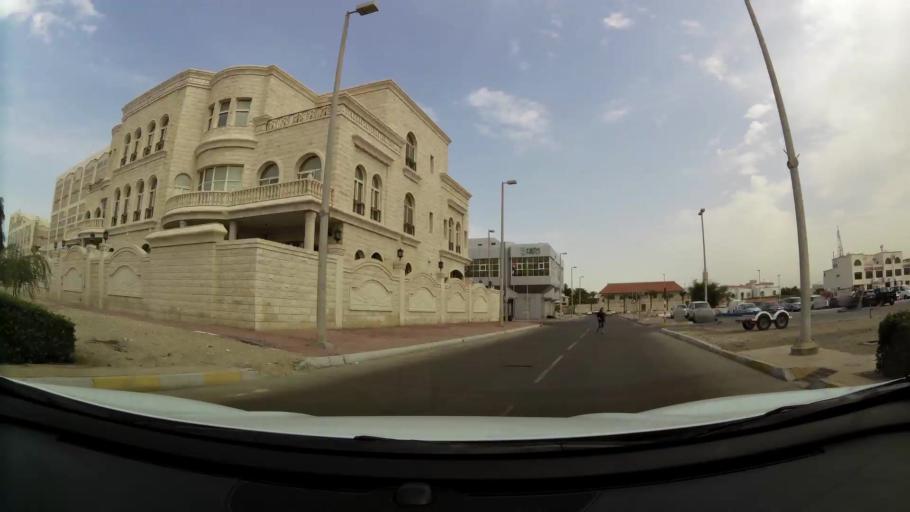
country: AE
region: Abu Dhabi
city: Abu Dhabi
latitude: 24.4592
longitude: 54.3476
